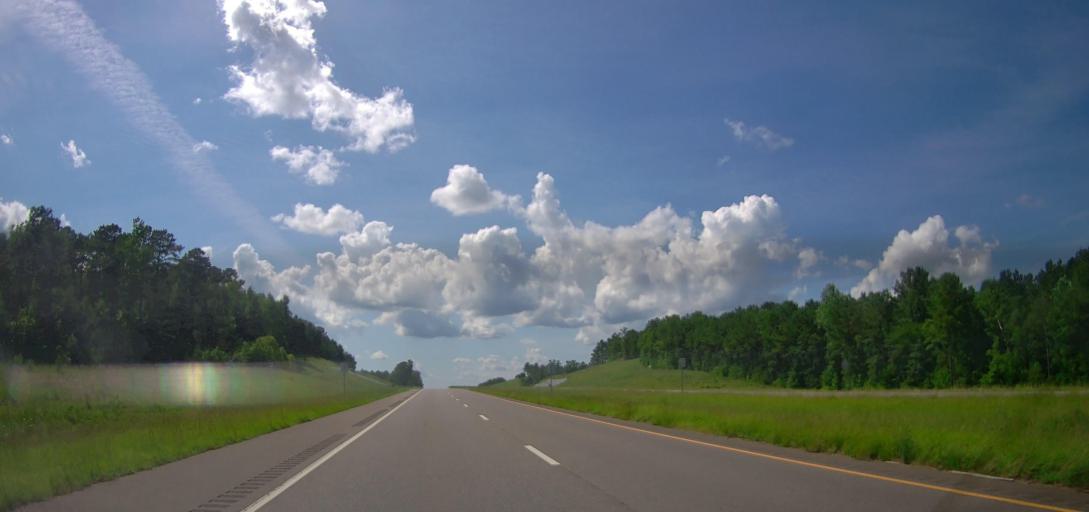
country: US
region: Alabama
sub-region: Pickens County
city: Reform
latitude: 33.3565
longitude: -87.9675
